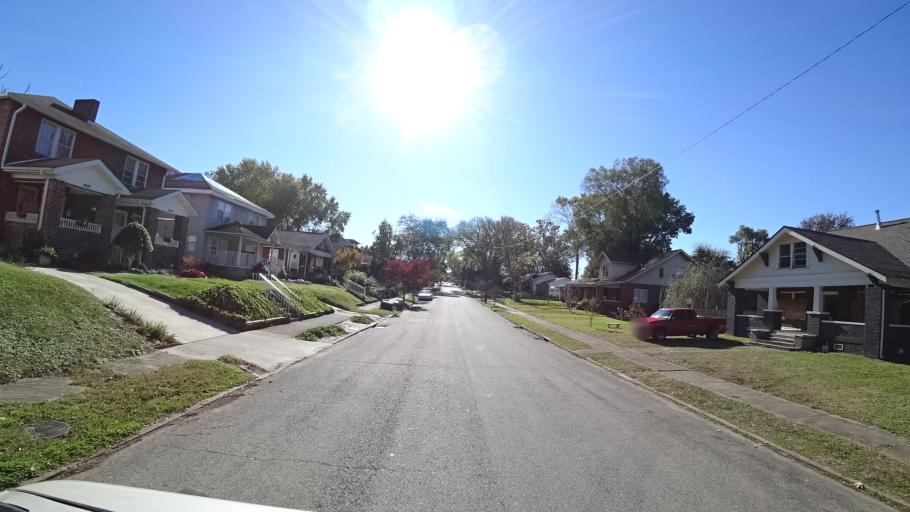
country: US
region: Tennessee
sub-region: Knox County
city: Knoxville
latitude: 35.9837
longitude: -83.8959
